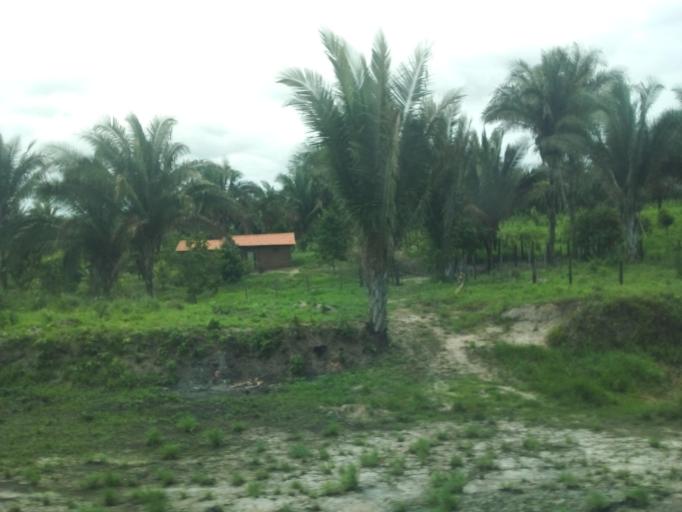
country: BR
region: Maranhao
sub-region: Santa Ines
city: Santa Ines
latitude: -3.7064
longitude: -45.9342
